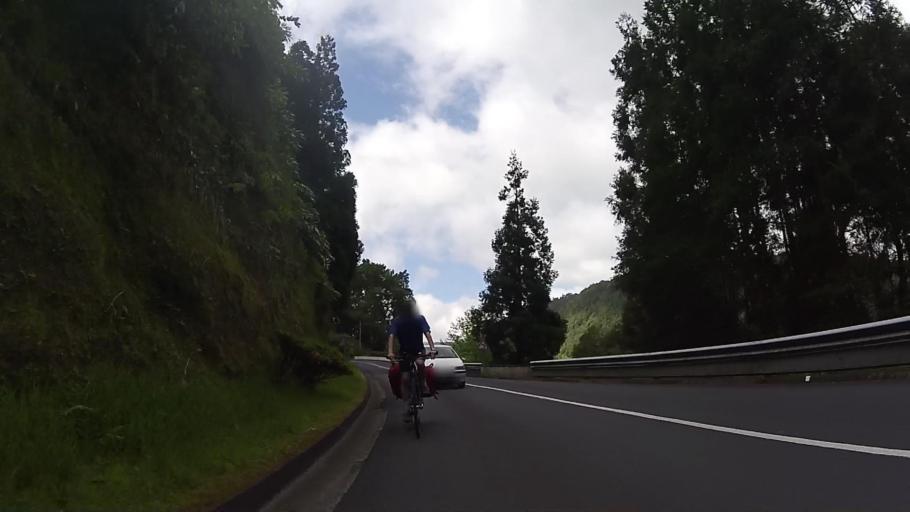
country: PT
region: Azores
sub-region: Povoacao
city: Furnas
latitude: 37.7666
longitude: -25.2884
